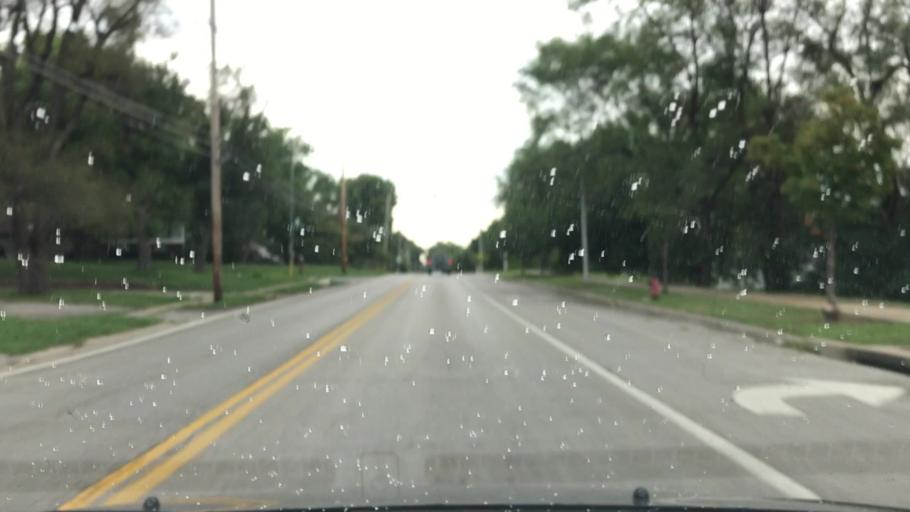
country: US
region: Missouri
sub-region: Jackson County
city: Grandview
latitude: 38.9300
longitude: -94.4934
